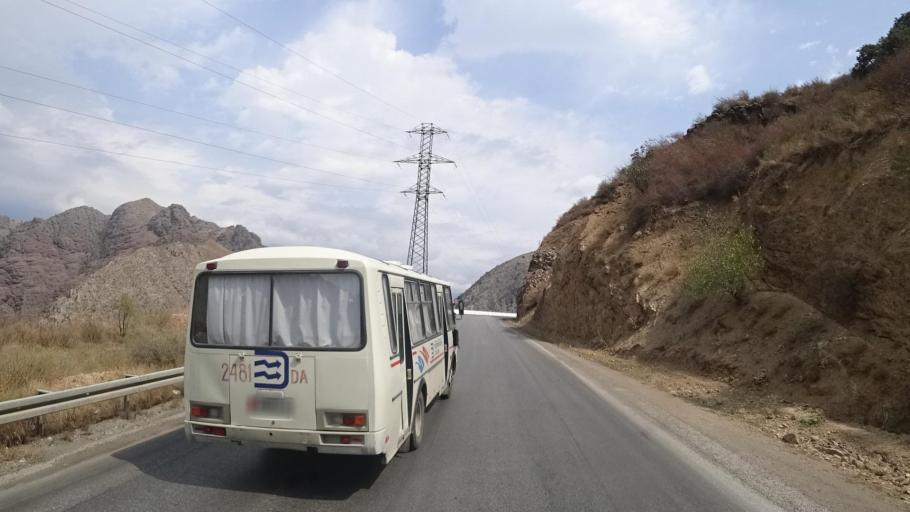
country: KG
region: Jalal-Abad
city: Tash-Kumyr
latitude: 41.5728
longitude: 72.5325
